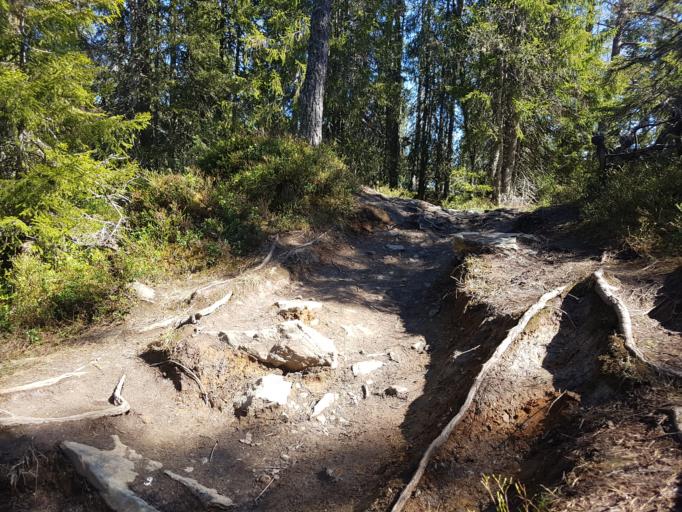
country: NO
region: Sor-Trondelag
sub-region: Trondheim
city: Trondheim
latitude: 63.4268
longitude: 10.3149
